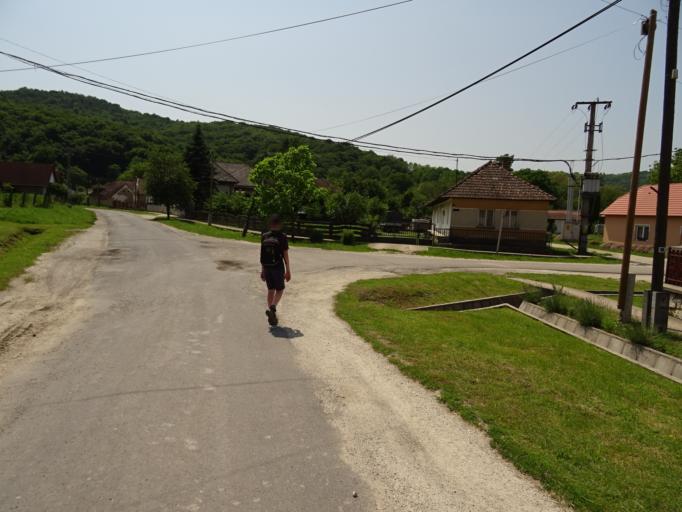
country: HU
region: Borsod-Abauj-Zemplen
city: Szendro
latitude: 48.5204
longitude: 20.7759
